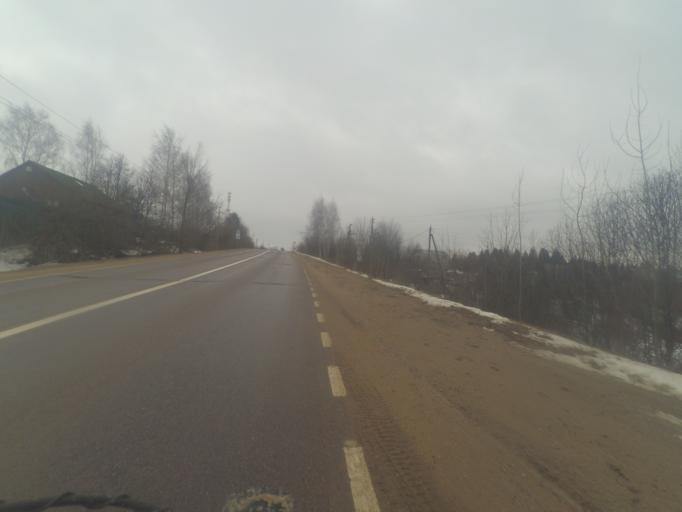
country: RU
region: Moskovskaya
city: Dedenevo
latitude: 56.2613
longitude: 37.5620
